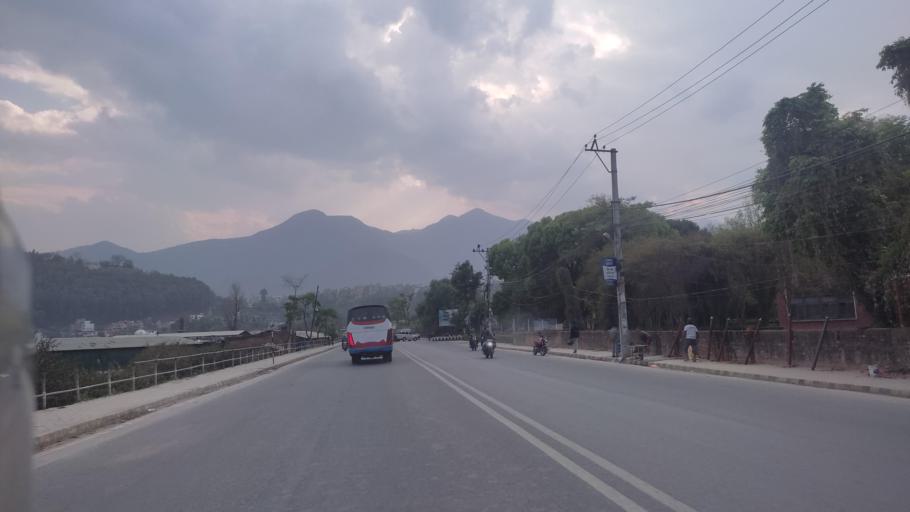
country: NP
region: Central Region
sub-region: Bagmati Zone
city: Patan
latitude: 27.6767
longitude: 85.2949
